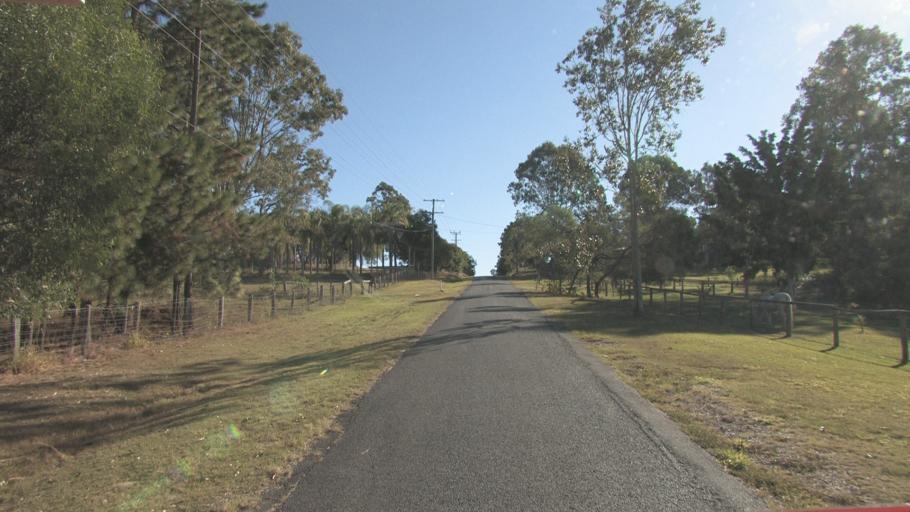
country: AU
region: Queensland
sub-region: Logan
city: Logan Reserve
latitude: -27.7360
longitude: 153.1071
